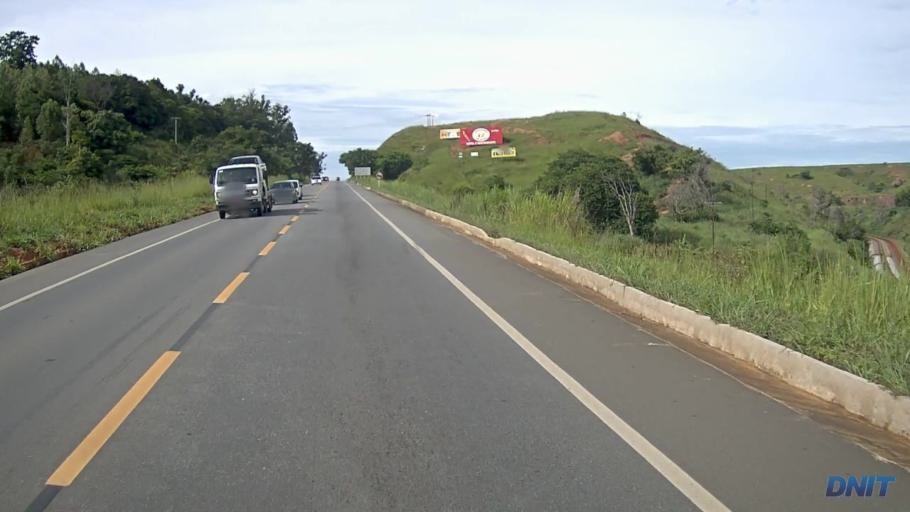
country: BR
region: Minas Gerais
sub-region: Belo Oriente
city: Belo Oriente
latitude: -19.2539
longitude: -42.3407
